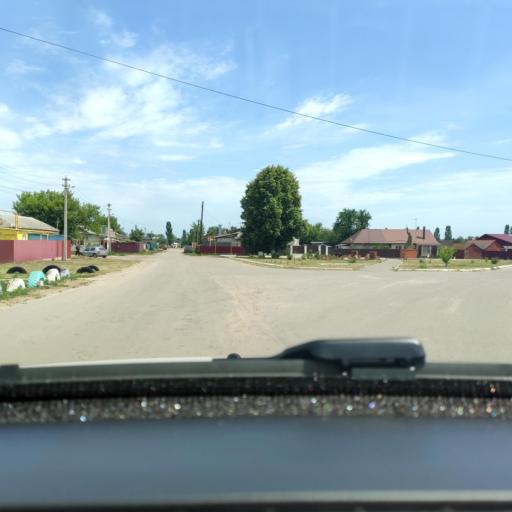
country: RU
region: Voronezj
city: Maslovka
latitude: 51.5054
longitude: 39.2962
